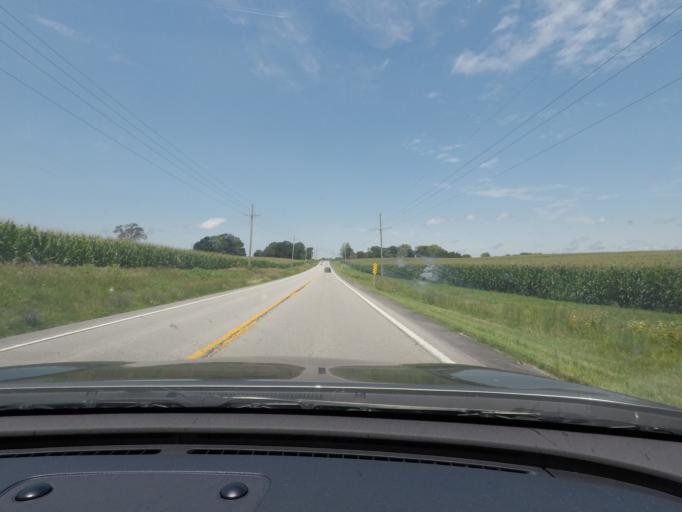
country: US
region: Missouri
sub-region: Saline County
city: Marshall
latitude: 39.1425
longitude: -93.2371
